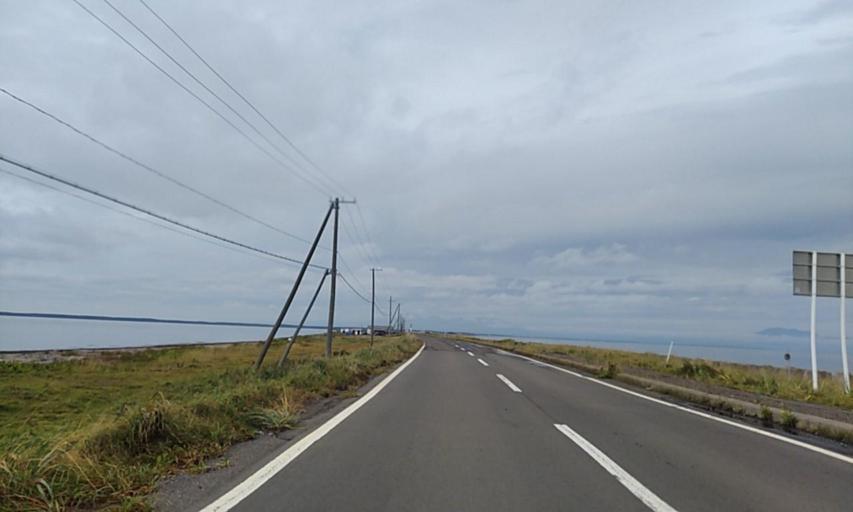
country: JP
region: Hokkaido
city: Shibetsu
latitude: 43.6116
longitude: 145.2632
